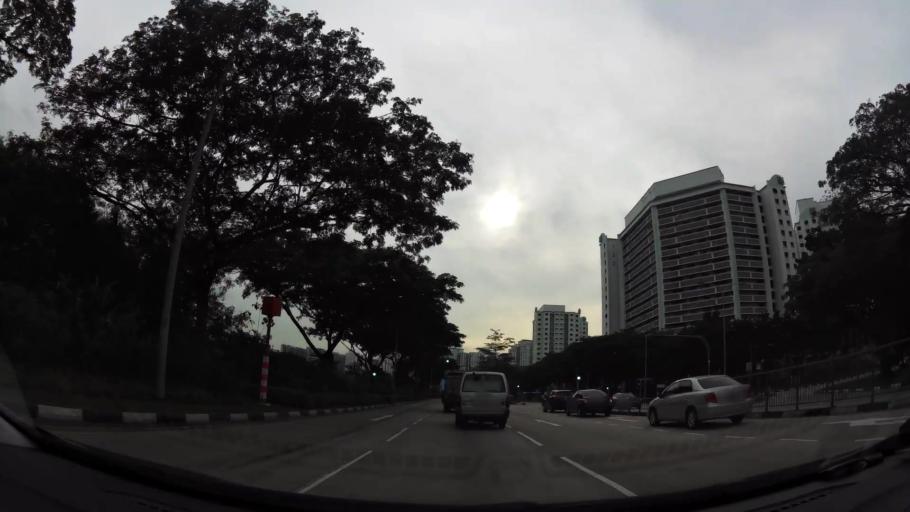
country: MY
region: Johor
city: Kampung Pasir Gudang Baru
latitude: 1.3866
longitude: 103.9079
